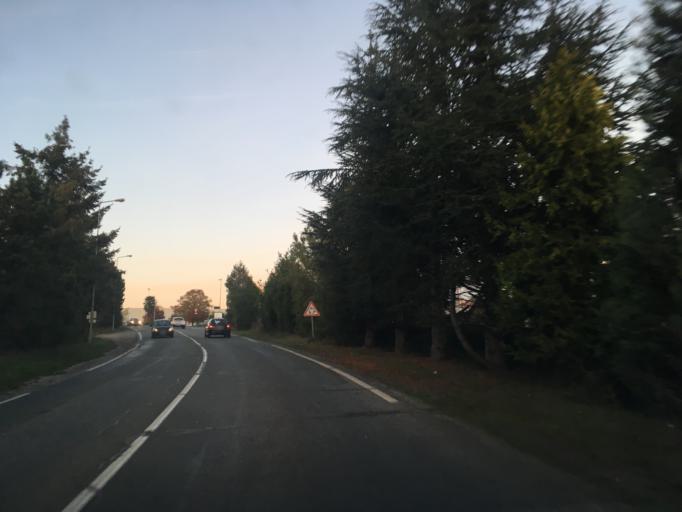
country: FR
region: Haute-Normandie
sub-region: Departement de l'Eure
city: Pacy-sur-Eure
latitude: 49.0105
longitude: 1.3926
